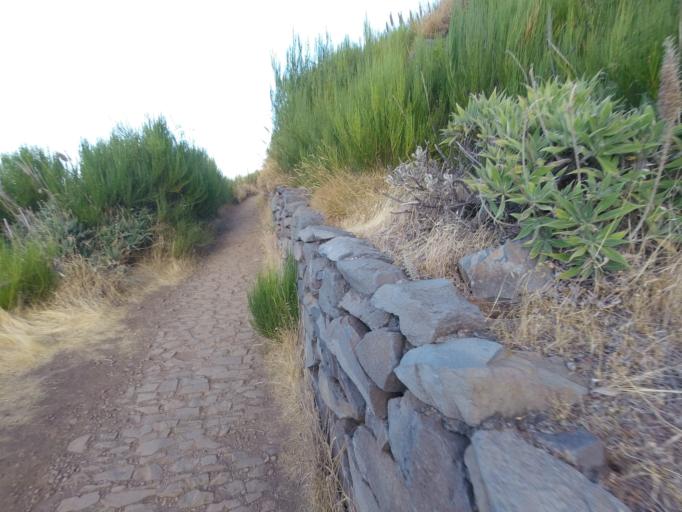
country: PT
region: Madeira
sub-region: Camara de Lobos
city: Curral das Freiras
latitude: 32.7384
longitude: -16.9342
